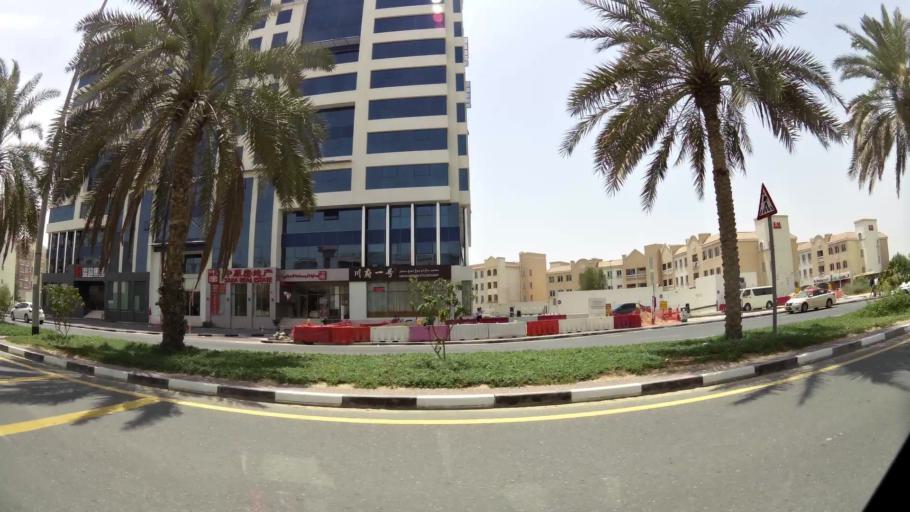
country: AE
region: Ash Shariqah
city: Sharjah
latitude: 25.1711
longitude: 55.4097
